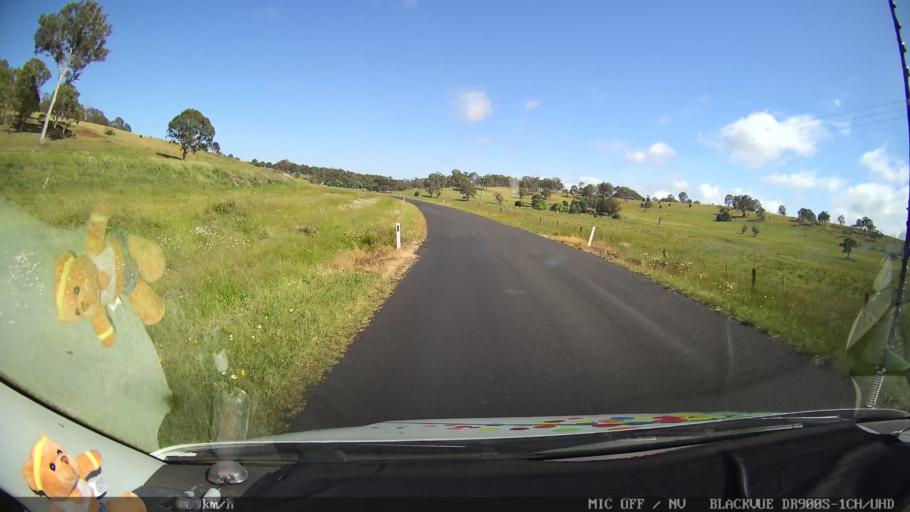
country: AU
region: New South Wales
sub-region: Guyra
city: Guyra
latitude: -30.1202
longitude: 151.6886
